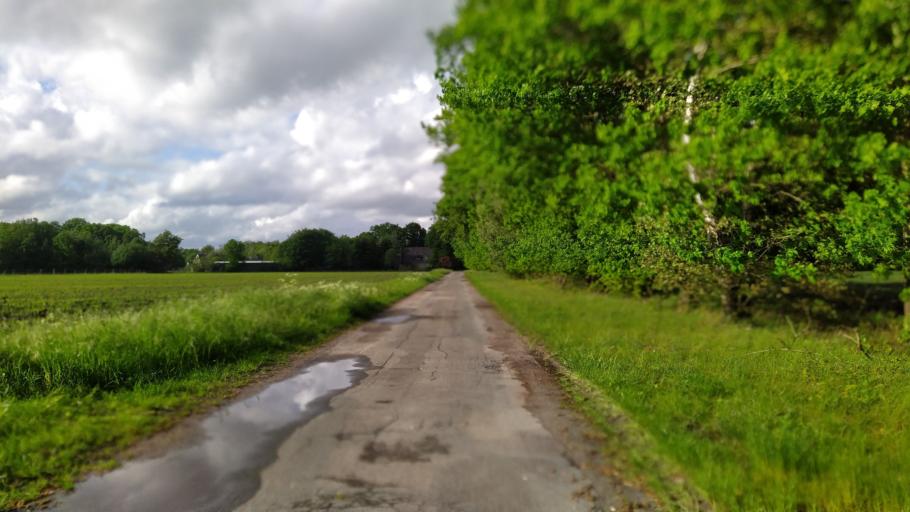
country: DE
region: Lower Saxony
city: Brest
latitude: 53.4292
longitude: 9.3544
